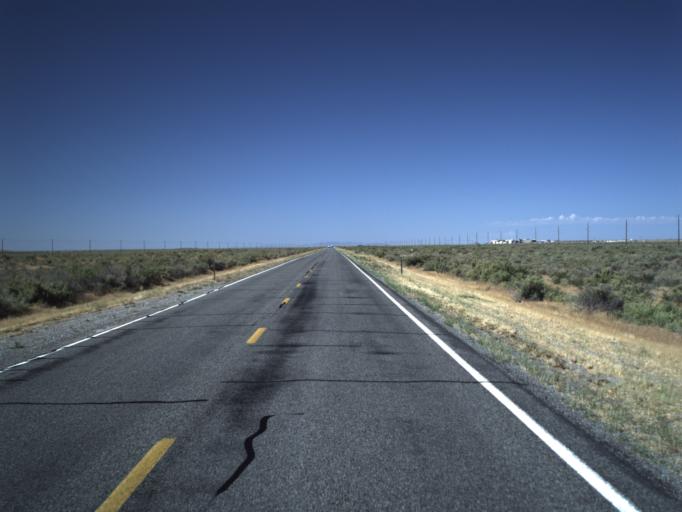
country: US
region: Utah
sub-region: Millard County
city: Delta
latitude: 39.4871
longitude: -112.4063
